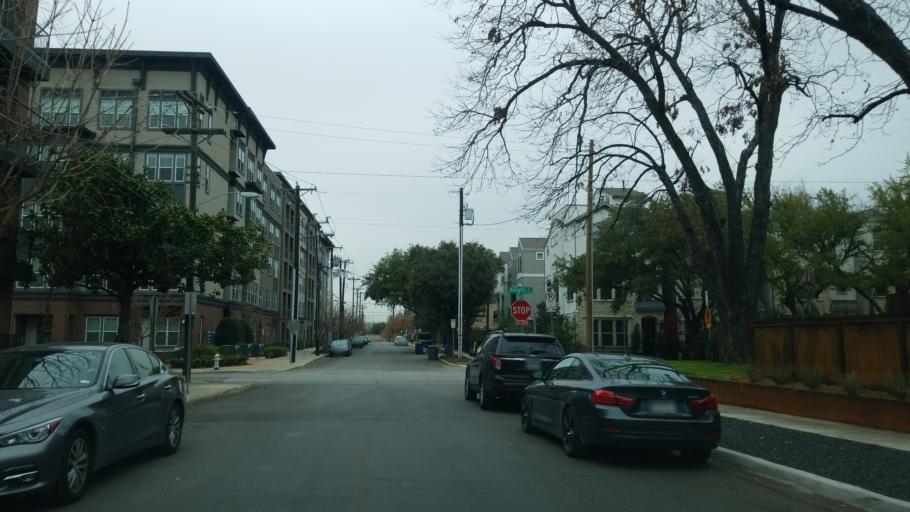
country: US
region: Texas
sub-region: Dallas County
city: Dallas
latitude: 32.8089
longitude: -96.8154
